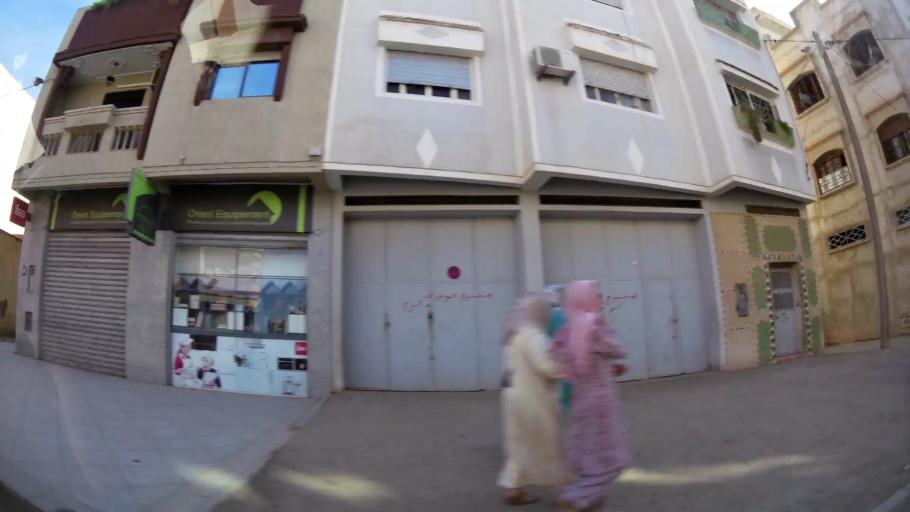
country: MA
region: Oriental
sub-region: Oujda-Angad
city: Oujda
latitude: 34.6710
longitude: -1.8990
